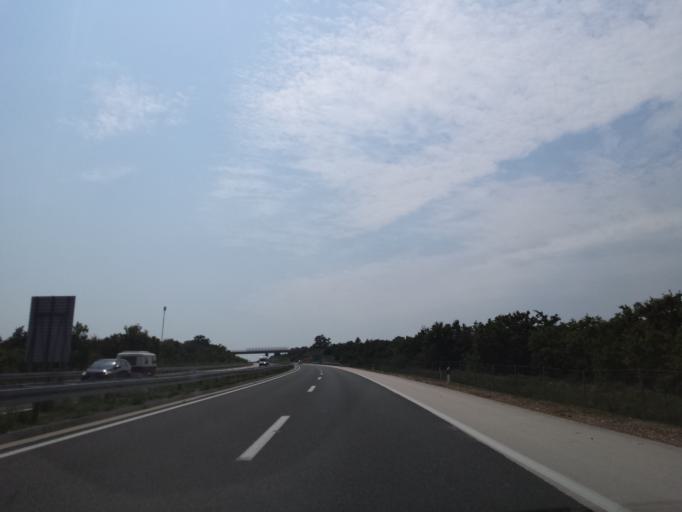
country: HR
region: Zadarska
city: Posedarje
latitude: 44.2106
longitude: 15.4465
